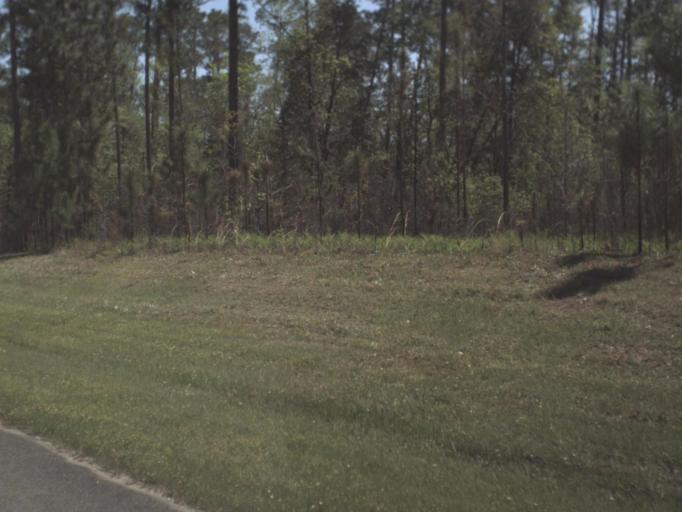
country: US
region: Florida
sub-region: Santa Rosa County
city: Point Baker
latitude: 30.8709
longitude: -86.9307
